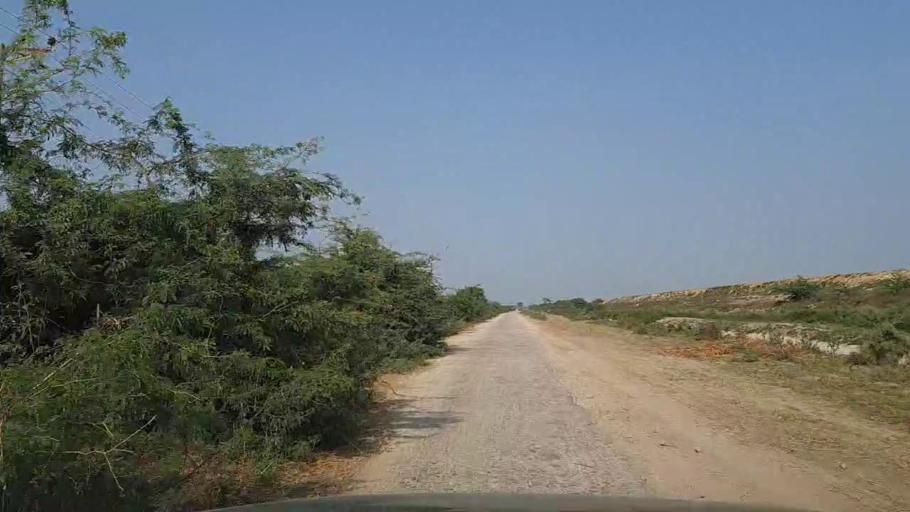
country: PK
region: Sindh
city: Chuhar Jamali
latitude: 24.5178
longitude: 67.9255
